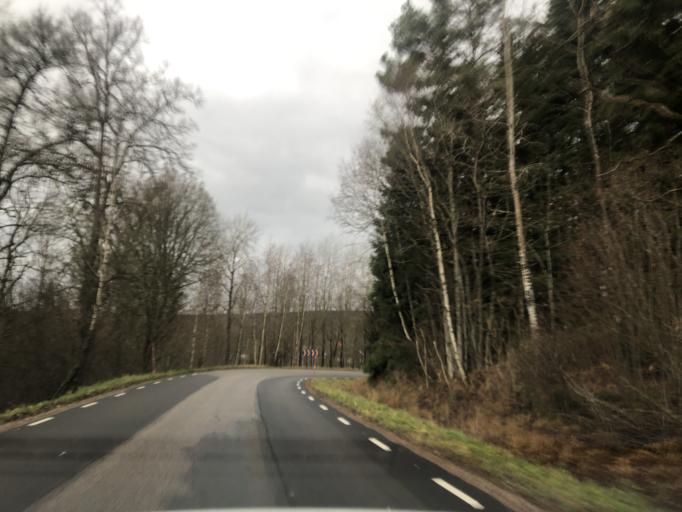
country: SE
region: Vaestra Goetaland
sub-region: Boras Kommun
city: Dalsjofors
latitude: 57.8245
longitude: 13.1923
